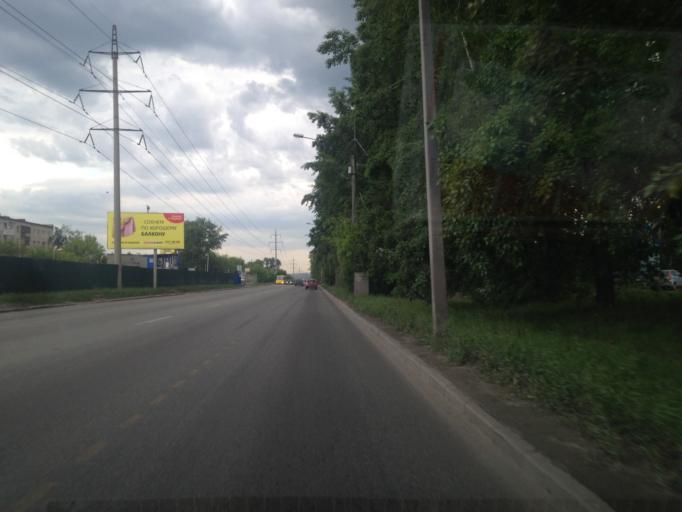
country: RU
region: Sverdlovsk
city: Sovkhoznyy
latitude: 56.7711
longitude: 60.5965
